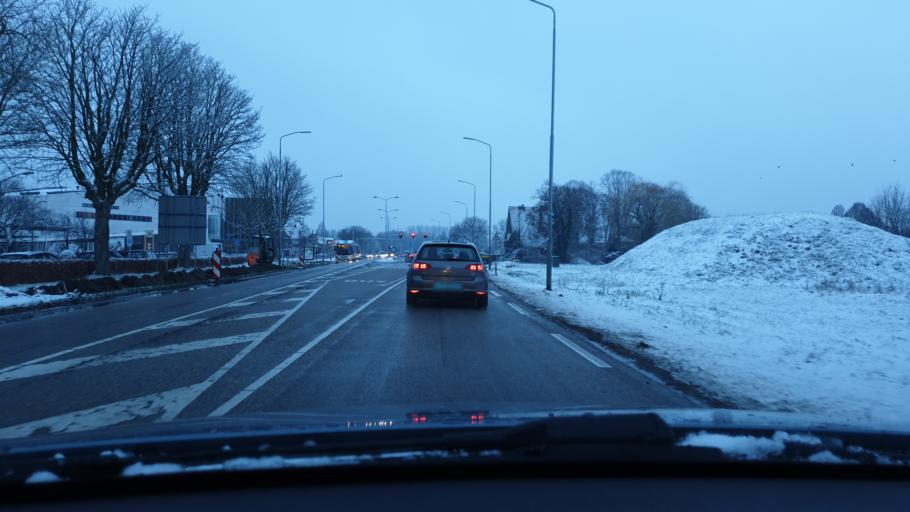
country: NL
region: North Brabant
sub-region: Gemeente Grave
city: Grave
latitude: 51.7617
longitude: 5.7337
